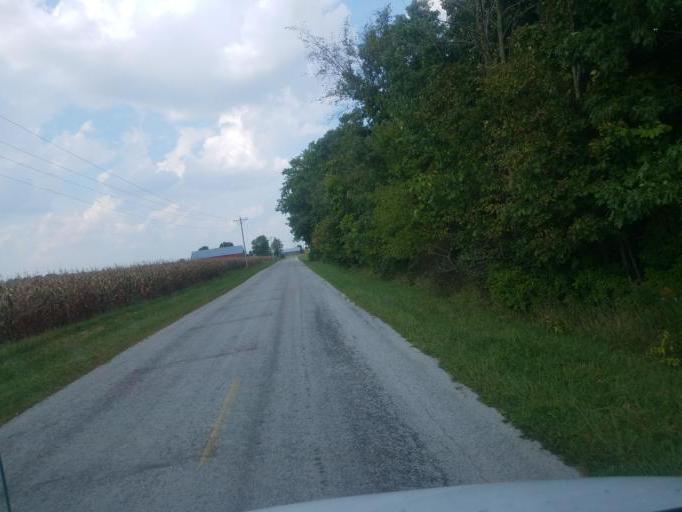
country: US
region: Ohio
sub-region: Hardin County
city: Kenton
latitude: 40.7348
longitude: -83.6022
